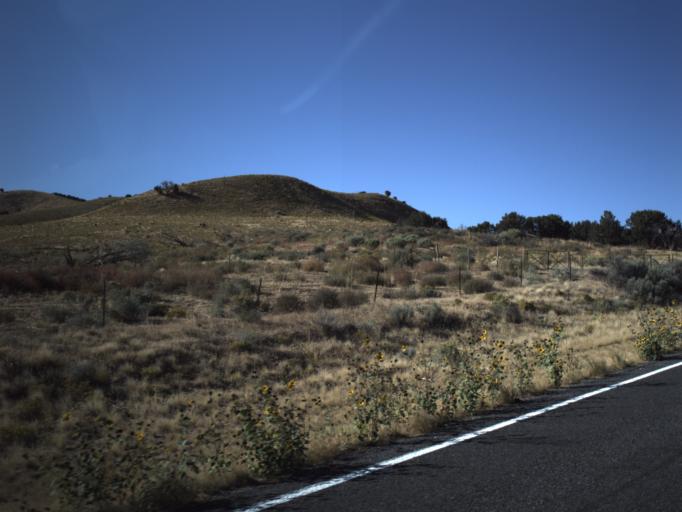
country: US
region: Utah
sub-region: Millard County
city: Delta
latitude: 39.4555
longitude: -112.3005
